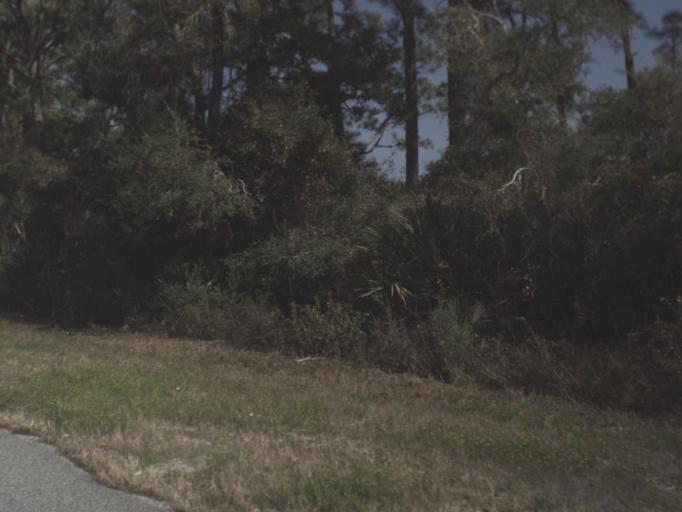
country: US
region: Florida
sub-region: Franklin County
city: Carrabelle
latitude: 29.7910
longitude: -84.7607
